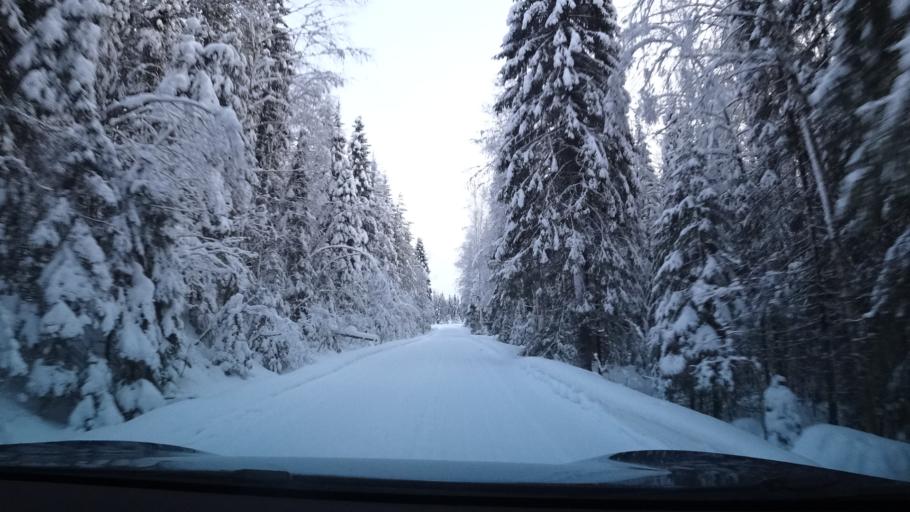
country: FI
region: North Karelia
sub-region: Pielisen Karjala
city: Lieksa
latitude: 63.1083
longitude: 29.7485
